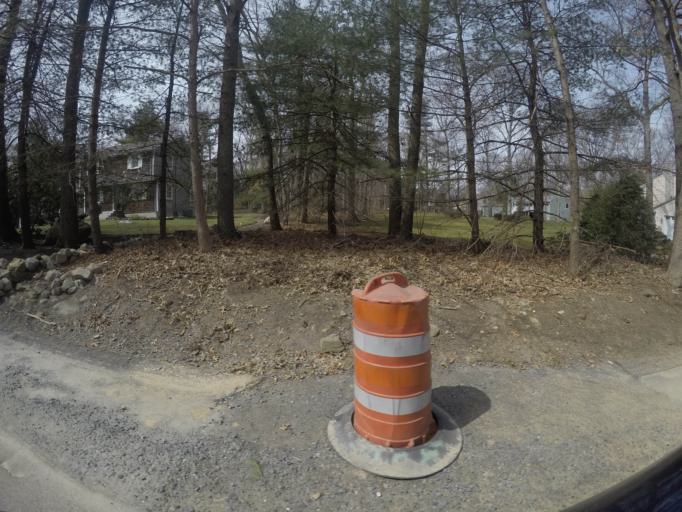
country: US
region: Massachusetts
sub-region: Bristol County
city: Easton
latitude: 42.0448
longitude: -71.1057
